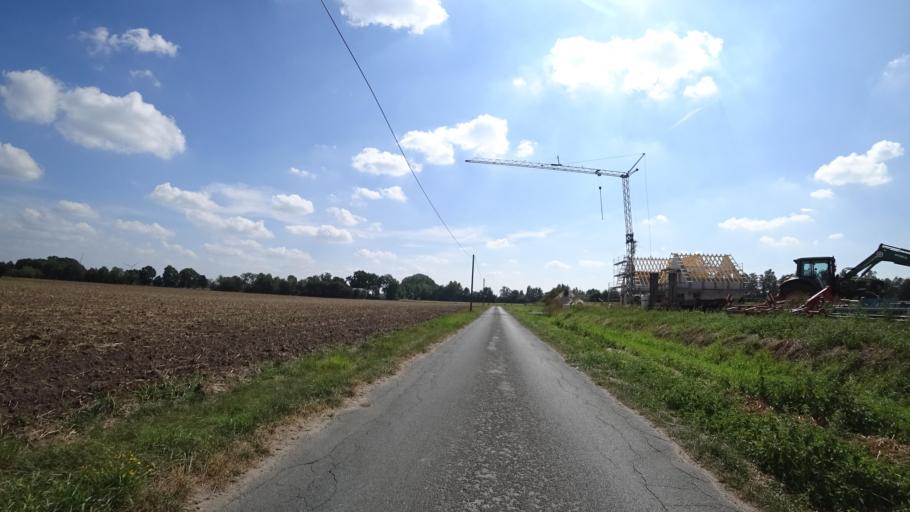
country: DE
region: North Rhine-Westphalia
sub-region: Regierungsbezirk Detmold
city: Rheda-Wiedenbruck
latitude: 51.8902
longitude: 8.2864
